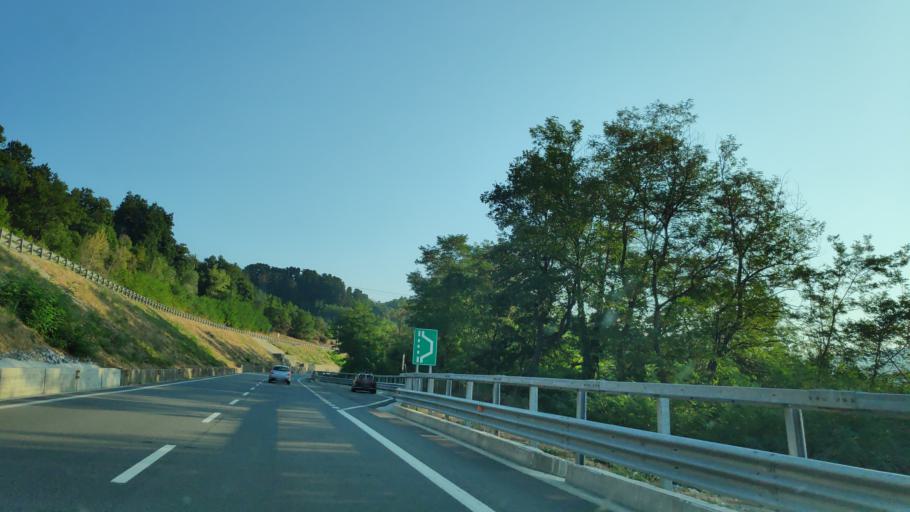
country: IT
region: Calabria
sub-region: Provincia di Cosenza
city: Belsito
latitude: 39.1605
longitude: 16.2870
